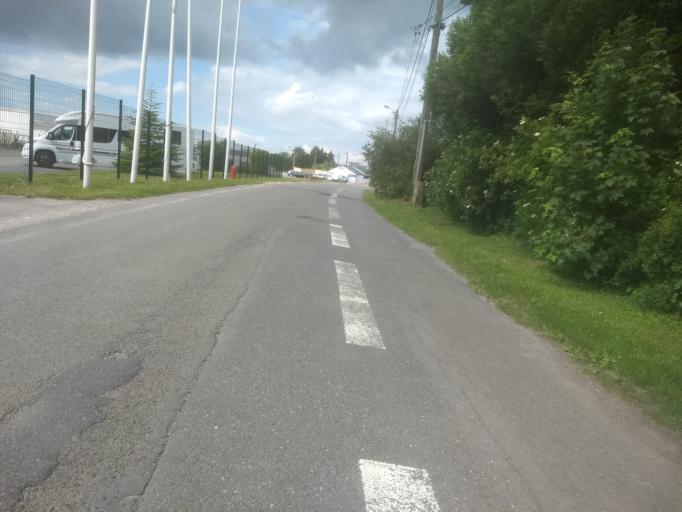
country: FR
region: Nord-Pas-de-Calais
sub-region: Departement du Pas-de-Calais
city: Dainville
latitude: 50.2725
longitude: 2.7209
